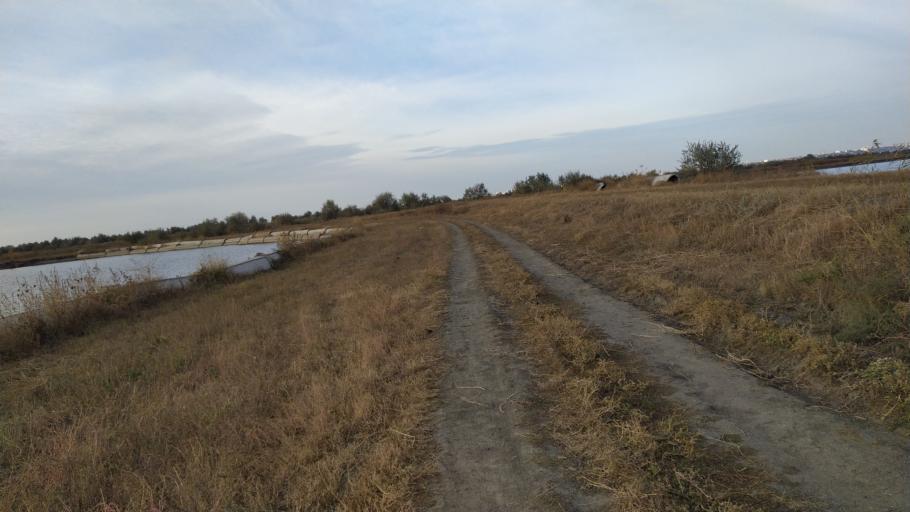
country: RU
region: Rostov
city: Kuleshovka
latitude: 47.1201
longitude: 39.6304
